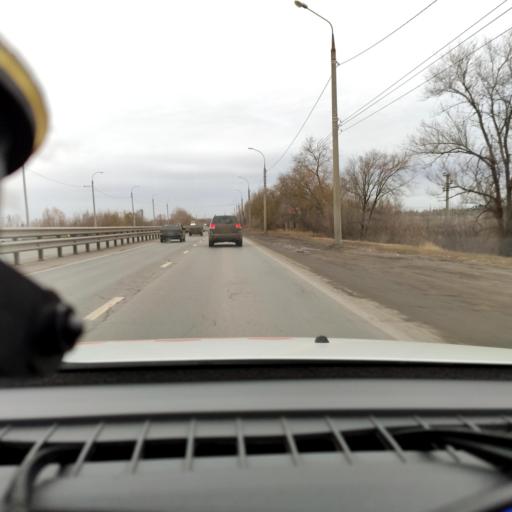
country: RU
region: Samara
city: Samara
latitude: 53.1162
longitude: 50.1664
